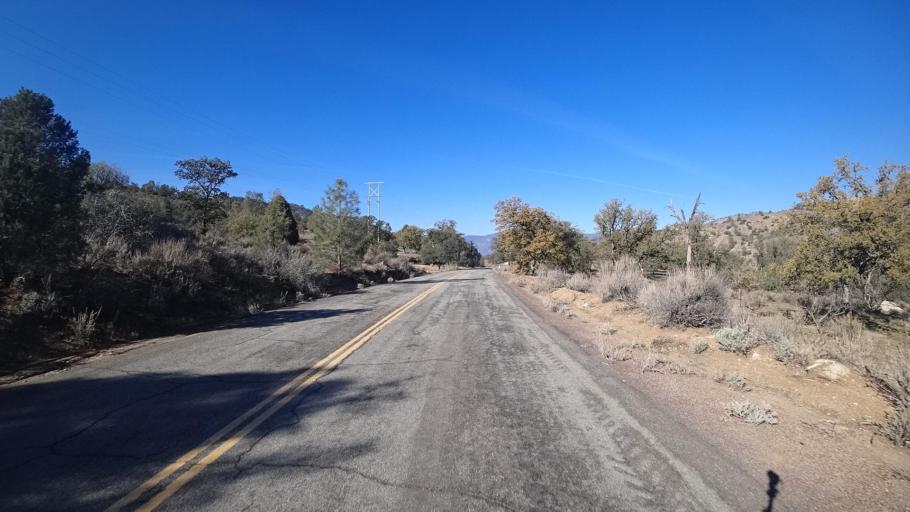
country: US
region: California
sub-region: Kern County
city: Bodfish
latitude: 35.3847
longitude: -118.4161
